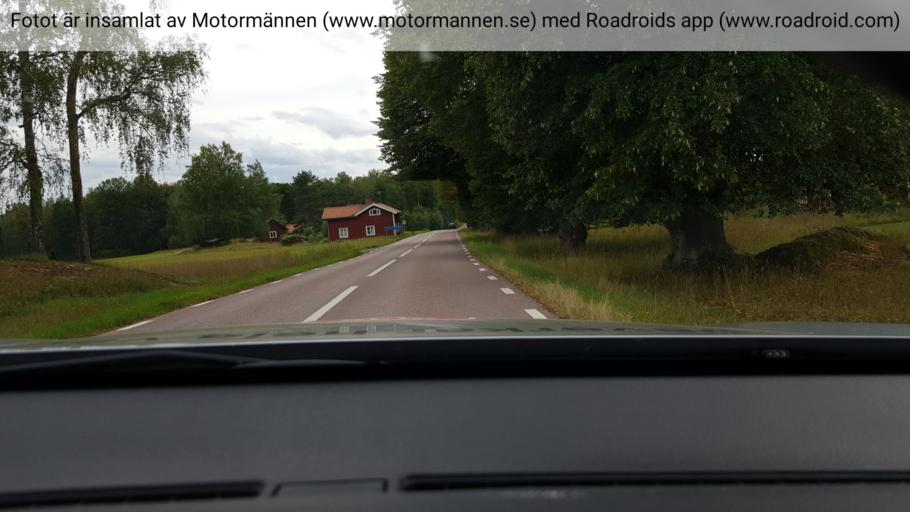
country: SE
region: Soedermanland
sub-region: Gnesta Kommun
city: Gnesta
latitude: 58.9518
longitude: 17.1273
